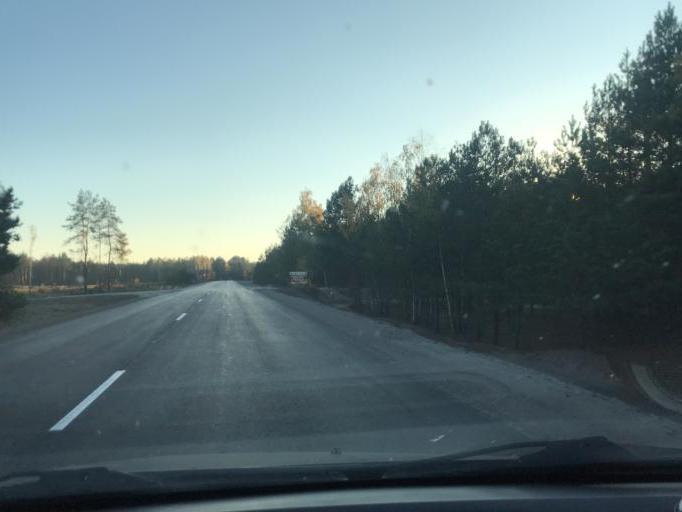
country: BY
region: Gomel
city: Brahin
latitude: 51.8627
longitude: 30.3717
